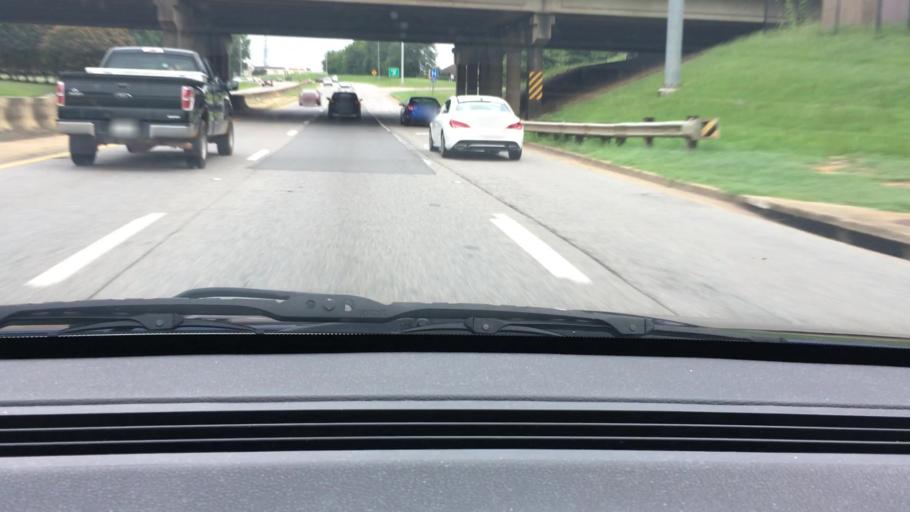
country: US
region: Alabama
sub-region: Tuscaloosa County
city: Tuscaloosa
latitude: 33.2058
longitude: -87.5245
